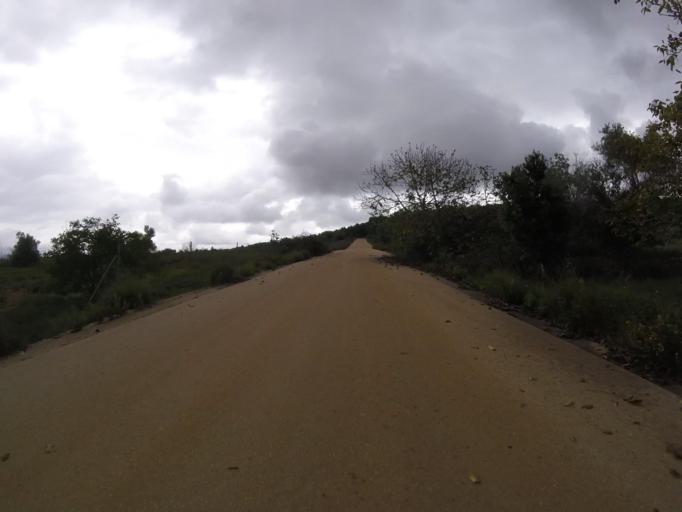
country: ES
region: Valencia
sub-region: Provincia de Castello
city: Benlloch
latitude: 40.2031
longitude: 0.0705
